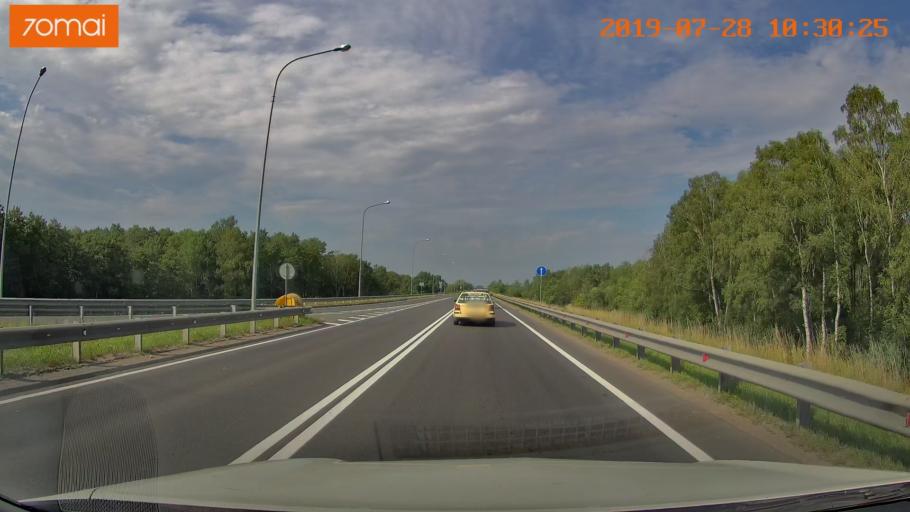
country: RU
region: Kaliningrad
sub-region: Gorod Kaliningrad
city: Kaliningrad
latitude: 54.7630
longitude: 20.4685
